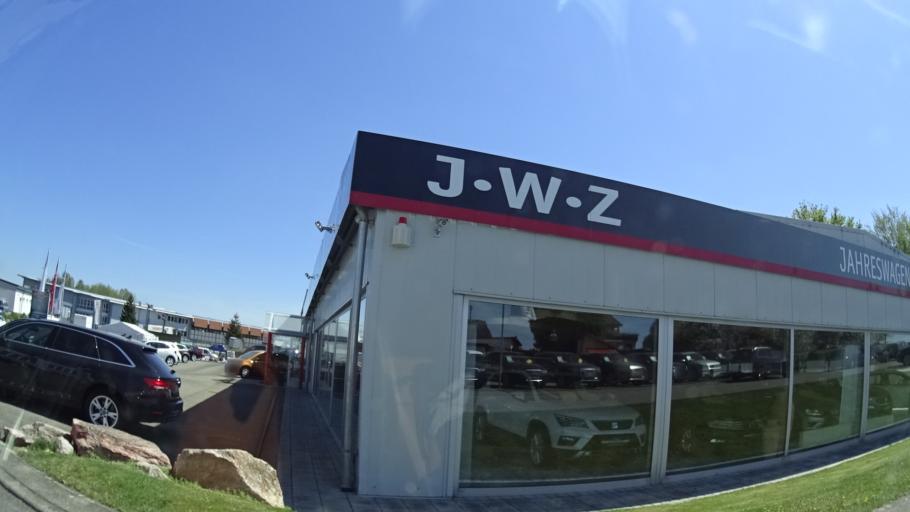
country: DE
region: Baden-Wuerttemberg
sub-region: Freiburg Region
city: Zimmern ob Rottweil
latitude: 48.1651
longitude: 8.6023
